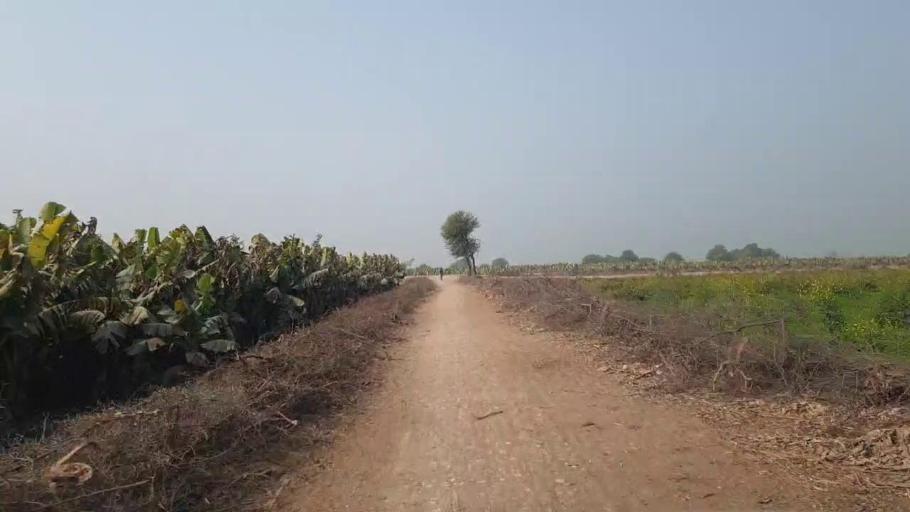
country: PK
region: Sindh
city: Hala
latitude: 25.8820
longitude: 68.3565
